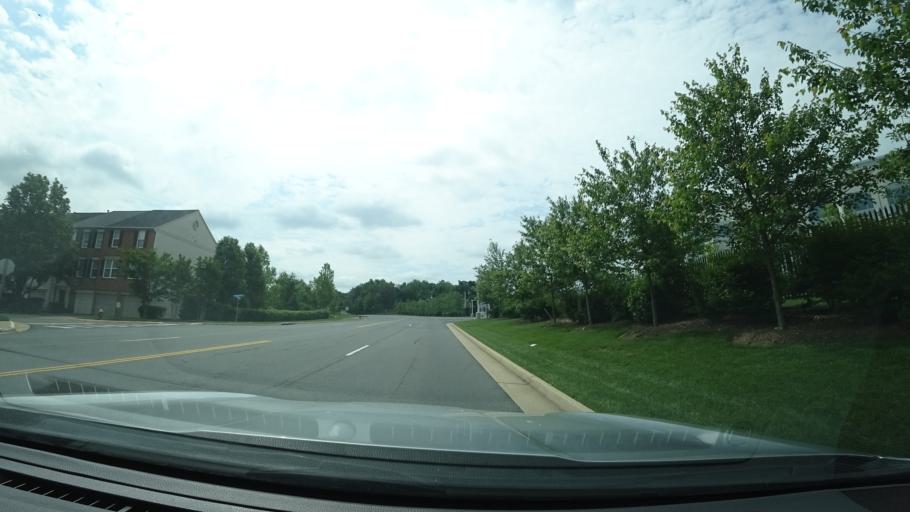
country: US
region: Virginia
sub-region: Loudoun County
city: Sterling
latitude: 38.9985
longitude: -77.4264
